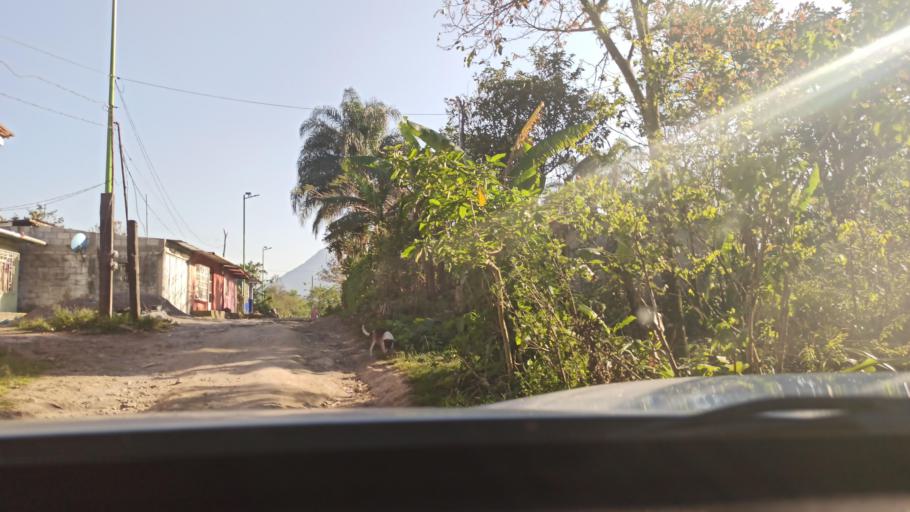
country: MX
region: Veracruz
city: Atzacan
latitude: 18.9048
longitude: -97.0879
